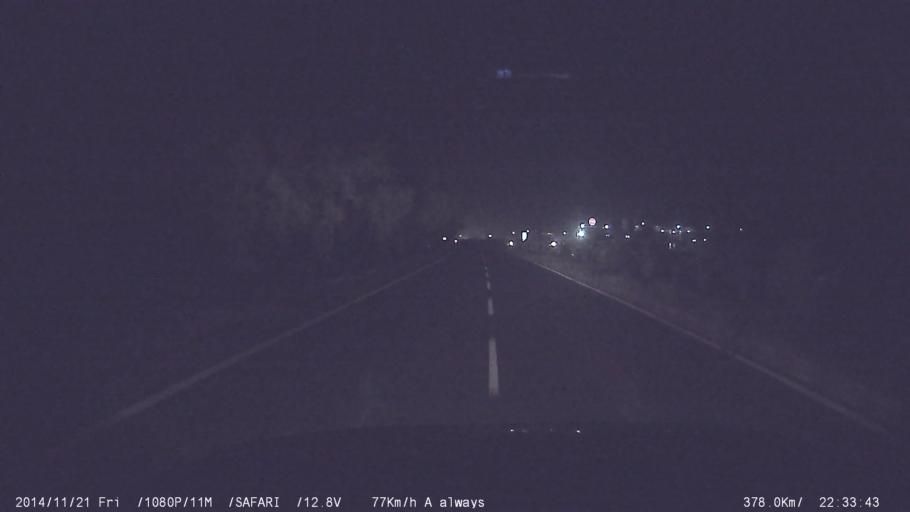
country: IN
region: Tamil Nadu
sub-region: Villupuram
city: Tindivanam
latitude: 12.3065
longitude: 79.7486
